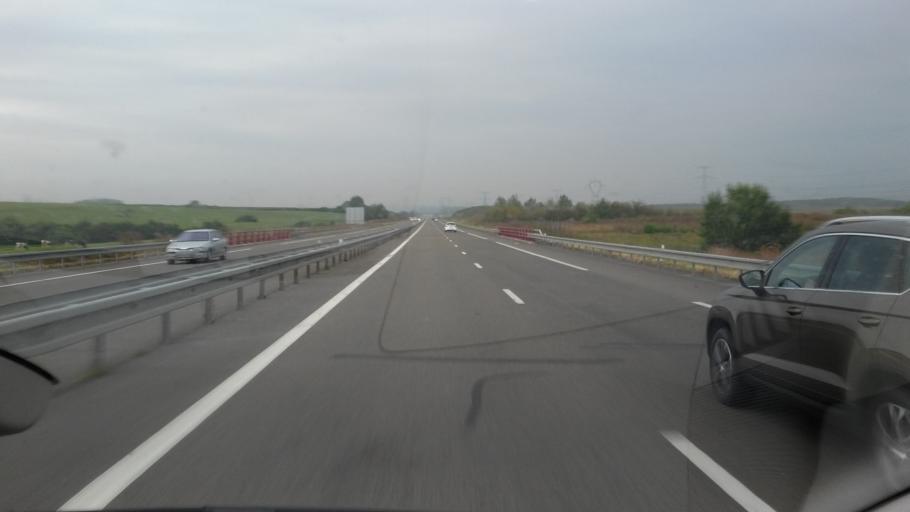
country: FR
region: Champagne-Ardenne
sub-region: Departement des Ardennes
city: Rethel
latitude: 49.5800
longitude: 4.4836
